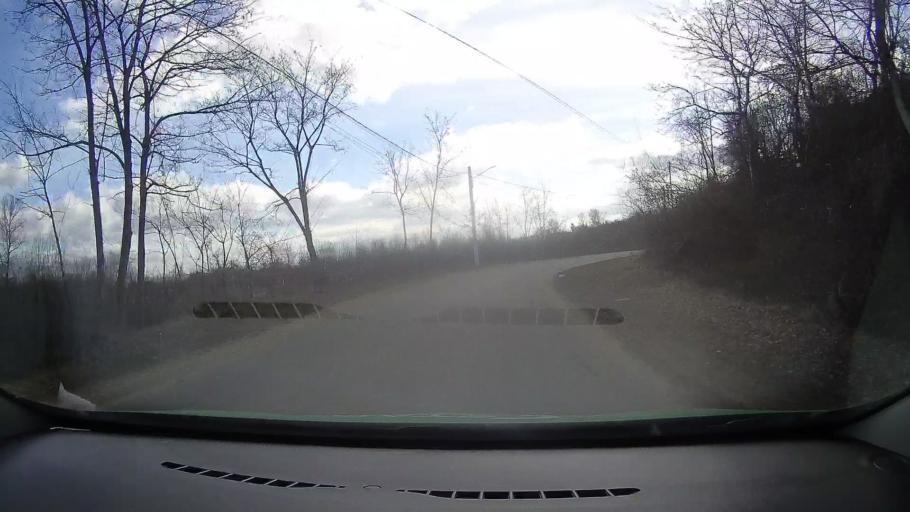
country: RO
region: Dambovita
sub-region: Comuna Sotanga
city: Teis
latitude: 44.9721
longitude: 25.3959
